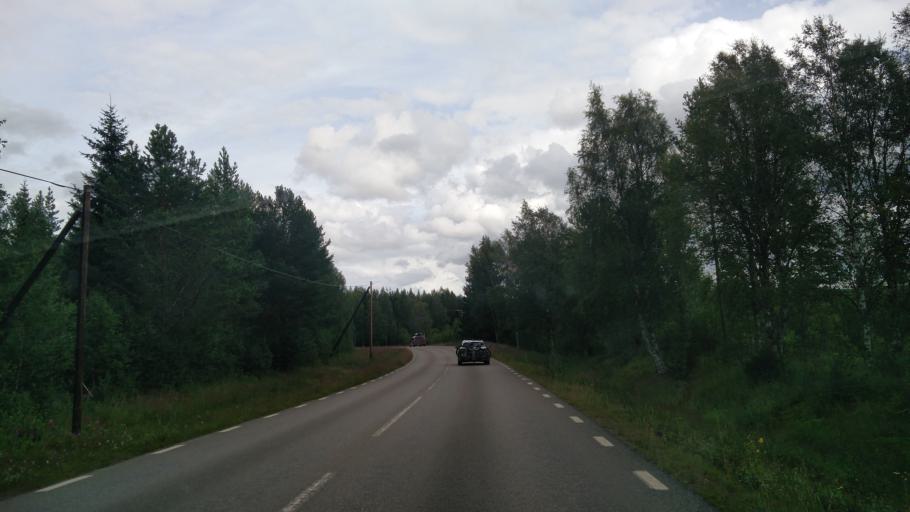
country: NO
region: Hedmark
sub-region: Trysil
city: Innbygda
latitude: 61.1660
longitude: 12.8342
